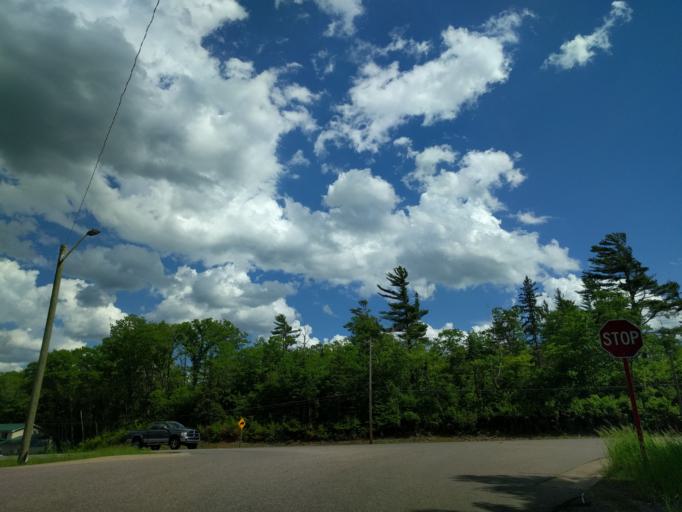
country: US
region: Michigan
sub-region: Marquette County
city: Trowbridge Park
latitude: 46.5375
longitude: -87.5025
